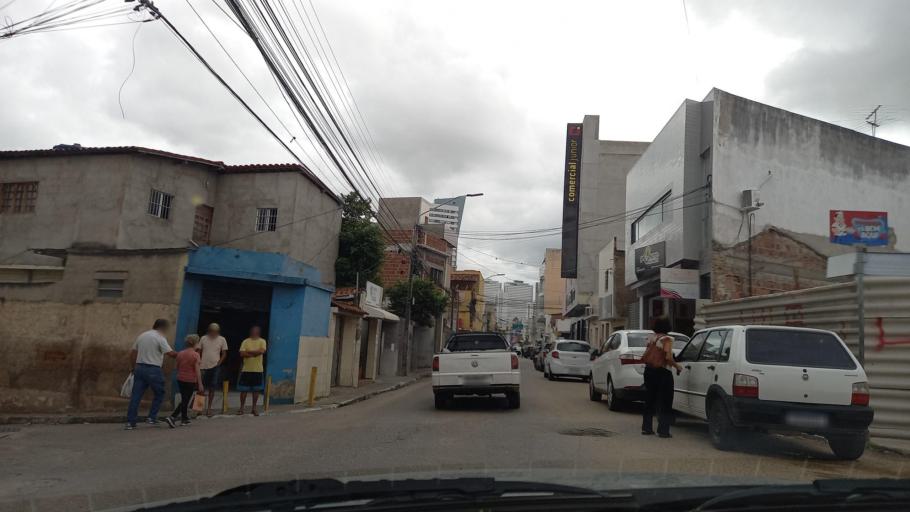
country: BR
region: Pernambuco
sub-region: Caruaru
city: Caruaru
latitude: -8.2766
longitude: -35.9658
